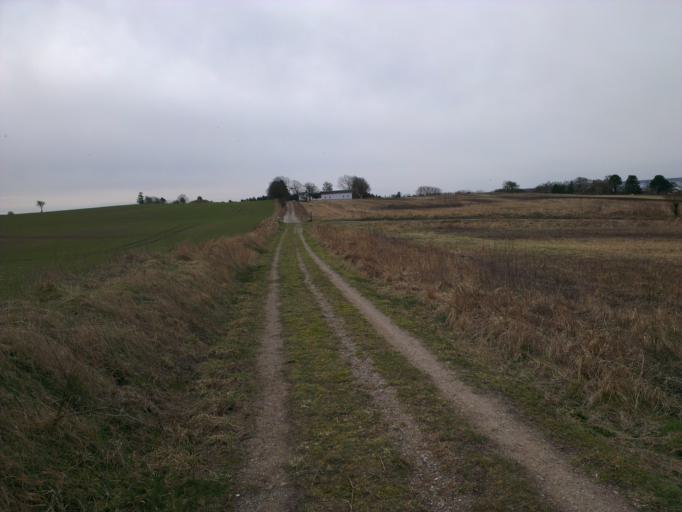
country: DK
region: Zealand
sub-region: Lejre Kommune
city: Ejby
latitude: 55.7709
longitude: 11.8659
